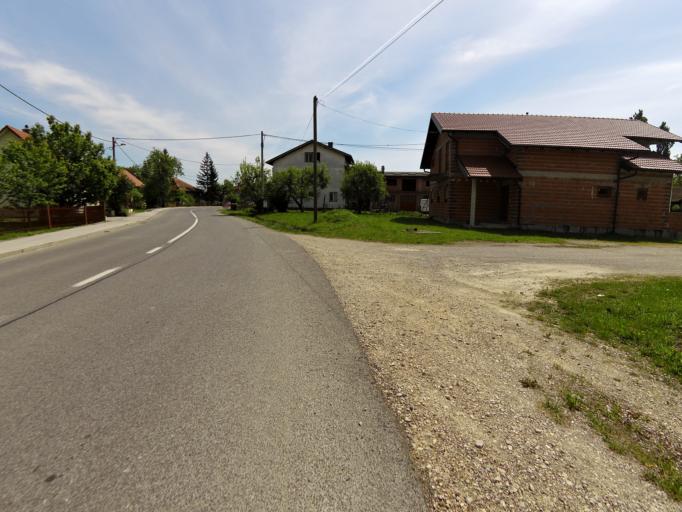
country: HR
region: Karlovacka
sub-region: Grad Karlovac
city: Karlovac
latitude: 45.5355
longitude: 15.5406
